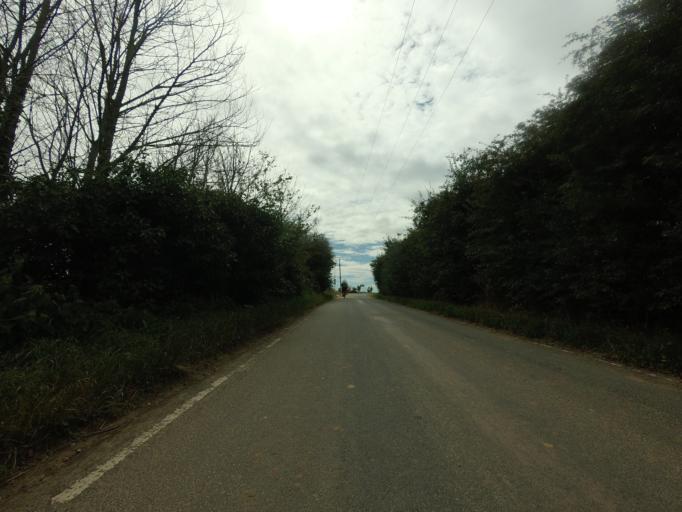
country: GB
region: England
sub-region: Kent
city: Hoo
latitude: 51.4316
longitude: 0.5928
